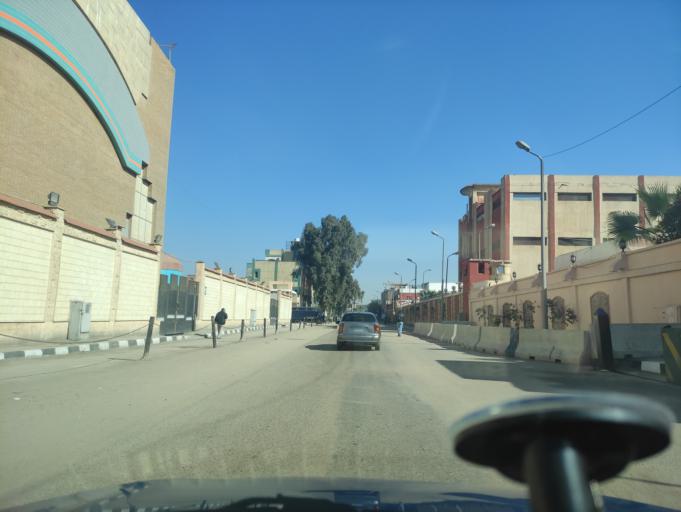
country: EG
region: Muhafazat al Qahirah
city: Cairo
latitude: 30.0535
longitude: 31.2759
